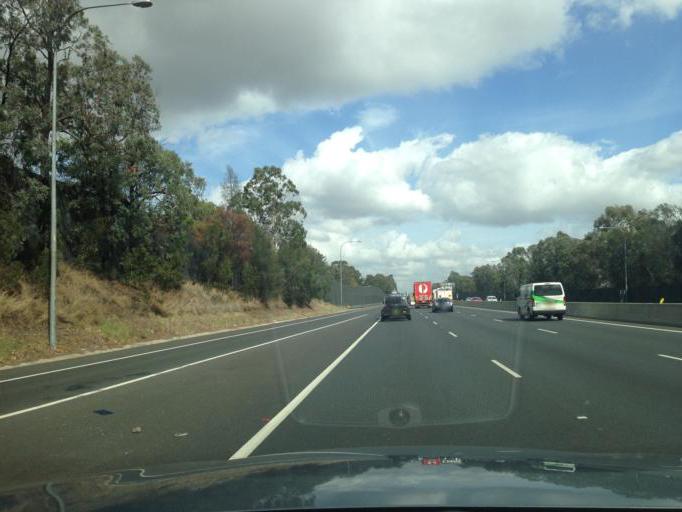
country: AU
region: New South Wales
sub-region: Bankstown
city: Revesby
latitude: -33.9406
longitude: 151.0159
